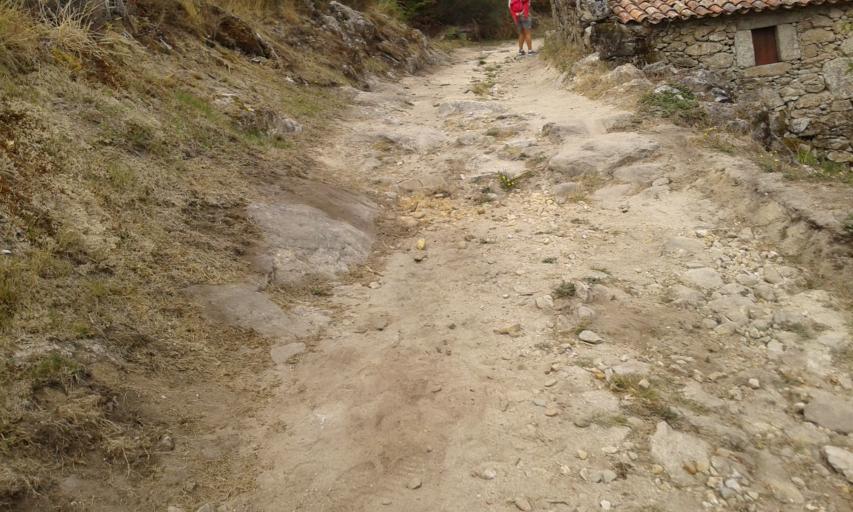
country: ES
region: Galicia
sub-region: Provincia de Pontevedra
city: O Rosal
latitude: 41.9569
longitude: -8.8396
